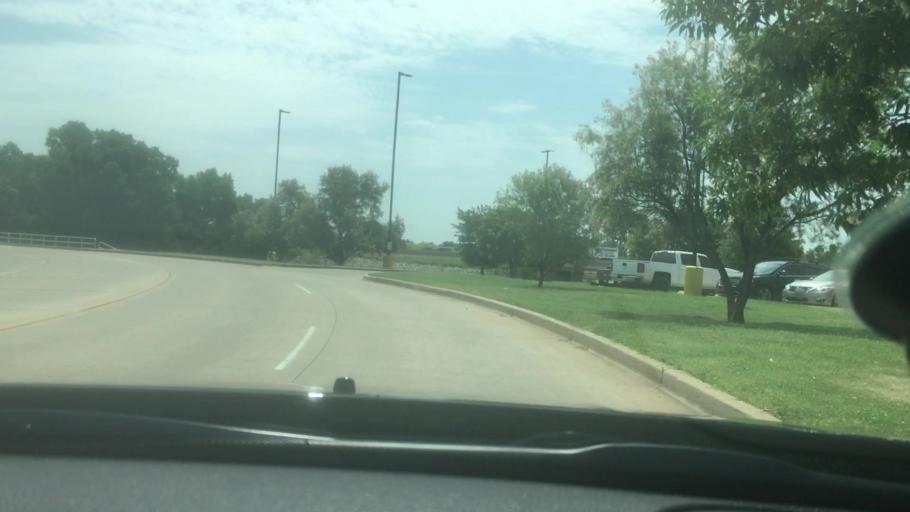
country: US
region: Oklahoma
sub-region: Oklahoma County
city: Bethany
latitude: 35.4619
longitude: -97.6344
